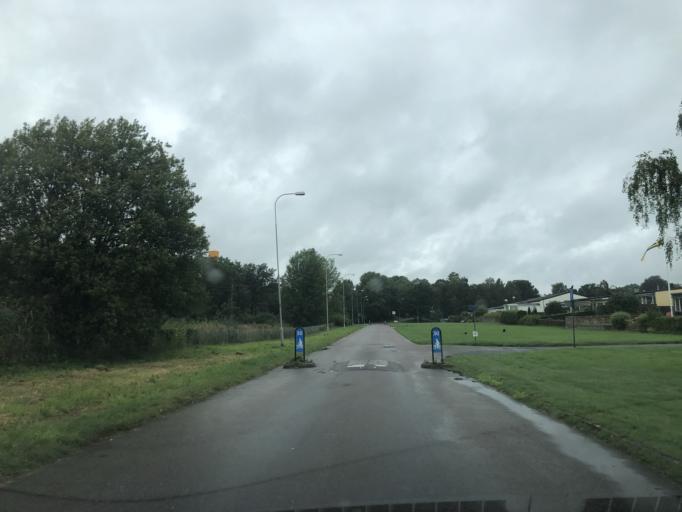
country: SE
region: Vaestra Goetaland
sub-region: Goteborg
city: Goeteborg
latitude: 57.7624
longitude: 11.9448
